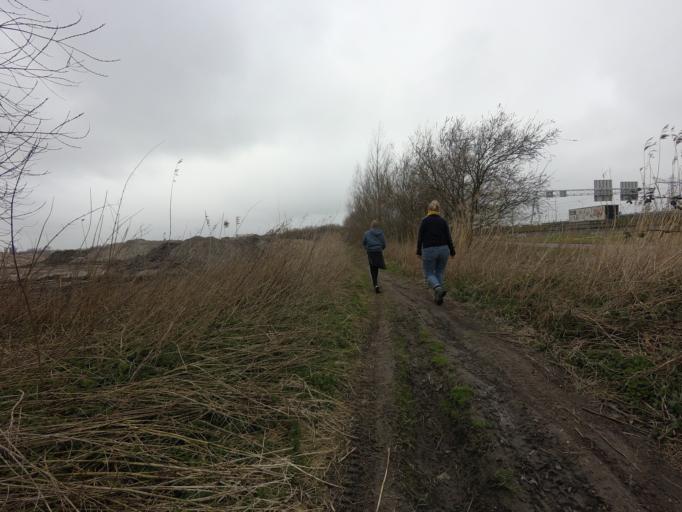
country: NL
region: North Holland
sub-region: Gemeente Landsmeer
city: Landsmeer
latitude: 52.4267
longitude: 4.8719
